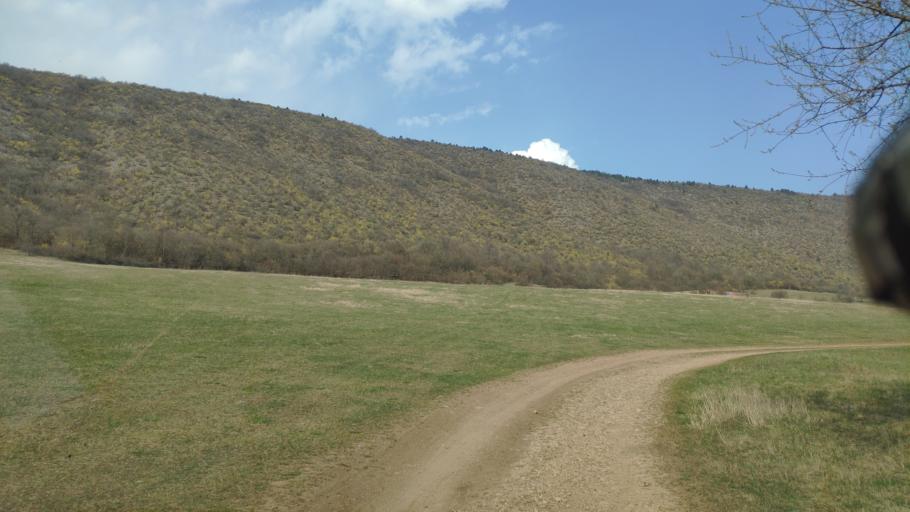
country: SK
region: Kosicky
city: Medzev
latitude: 48.6225
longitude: 20.8921
